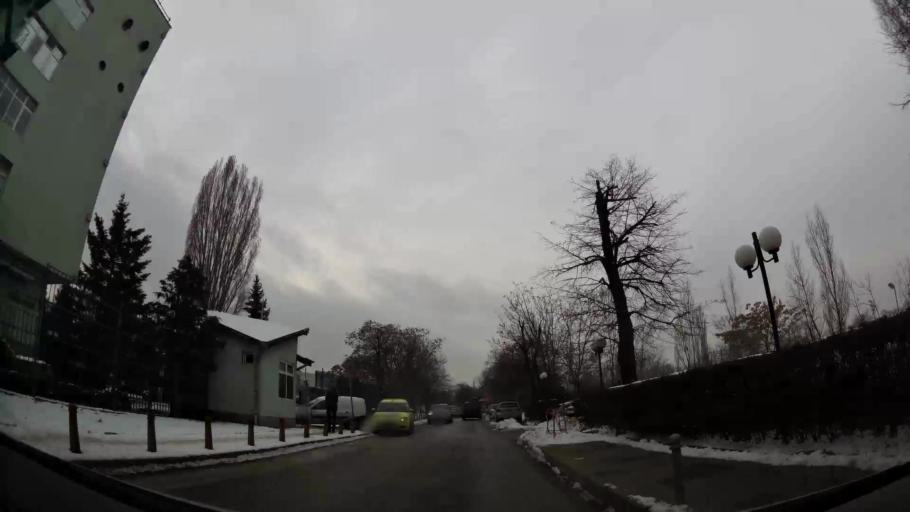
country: BG
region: Sofia-Capital
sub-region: Stolichna Obshtina
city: Sofia
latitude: 42.7170
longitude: 23.2972
